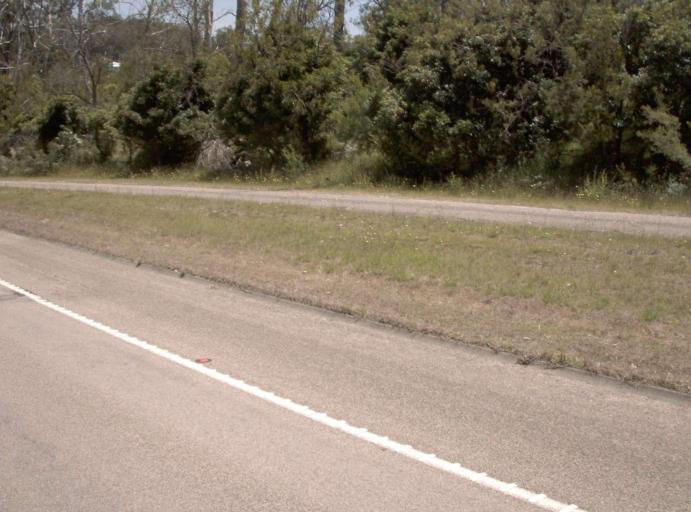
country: AU
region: Victoria
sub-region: East Gippsland
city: Bairnsdale
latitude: -37.7262
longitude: 147.7986
